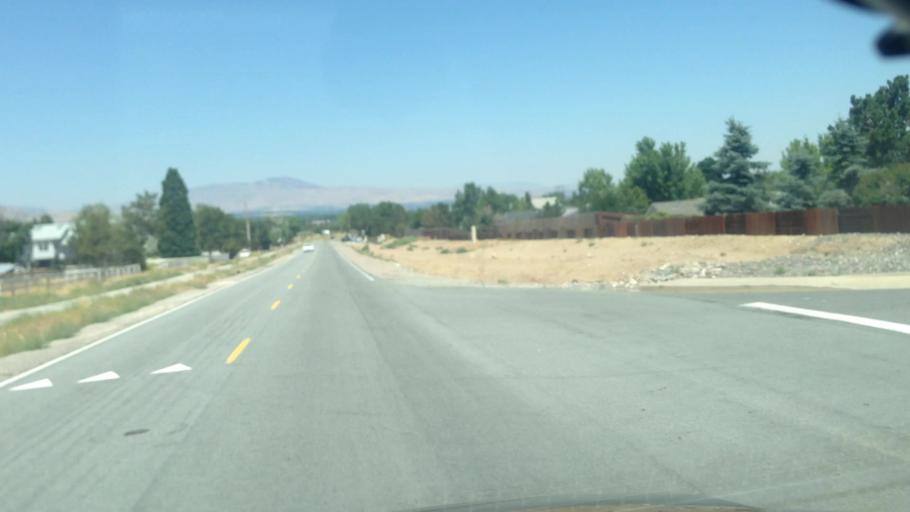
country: US
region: Nevada
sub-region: Storey County
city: Virginia City
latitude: 39.3927
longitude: -119.7321
